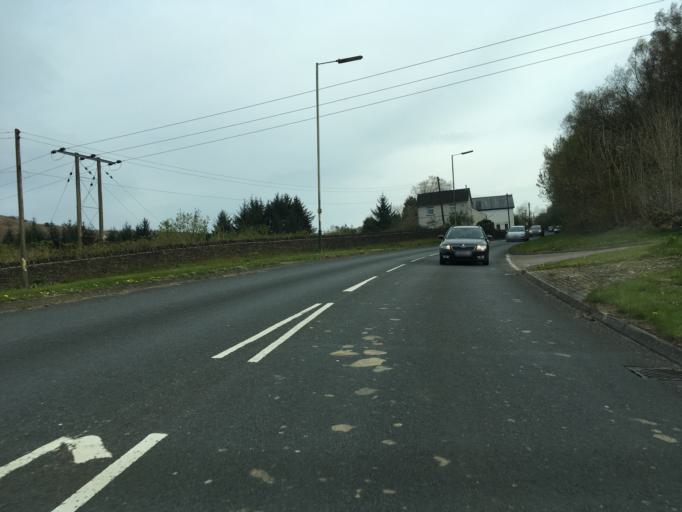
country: GB
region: Wales
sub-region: Caerphilly County Borough
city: Caerphilly
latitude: 51.5638
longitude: -3.2309
